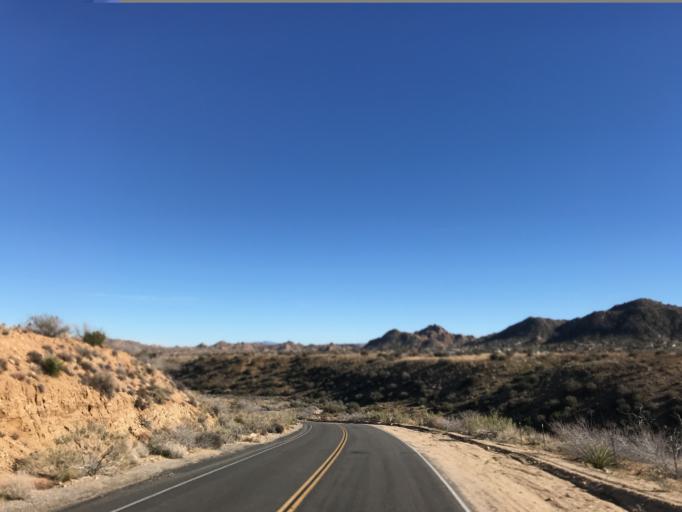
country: US
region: California
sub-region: San Bernardino County
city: Yucca Valley
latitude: 34.1621
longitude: -116.5138
